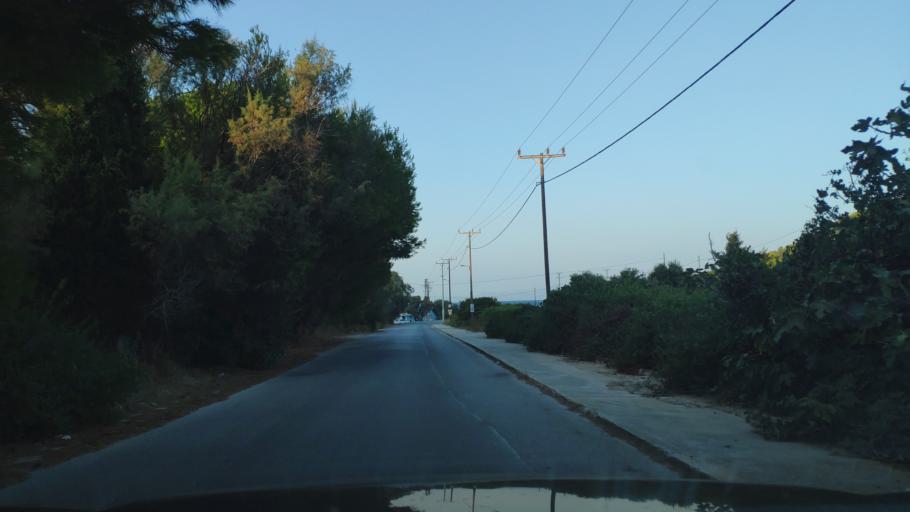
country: GR
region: Attica
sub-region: Nomarchia Anatolikis Attikis
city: Limin Mesoyaias
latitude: 37.9198
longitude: 24.0128
